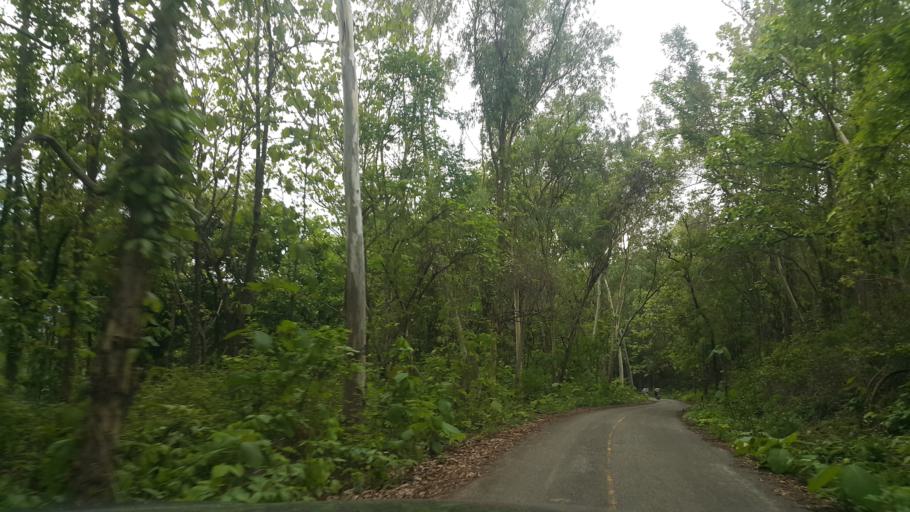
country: TH
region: Chiang Mai
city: Mae On
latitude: 18.7211
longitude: 99.2328
